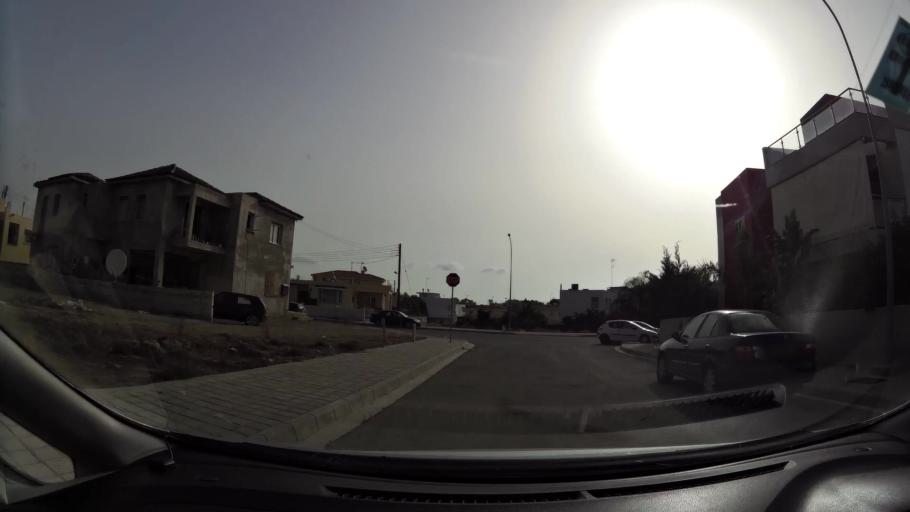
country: CY
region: Lefkosia
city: Geri
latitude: 35.0707
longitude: 33.3851
